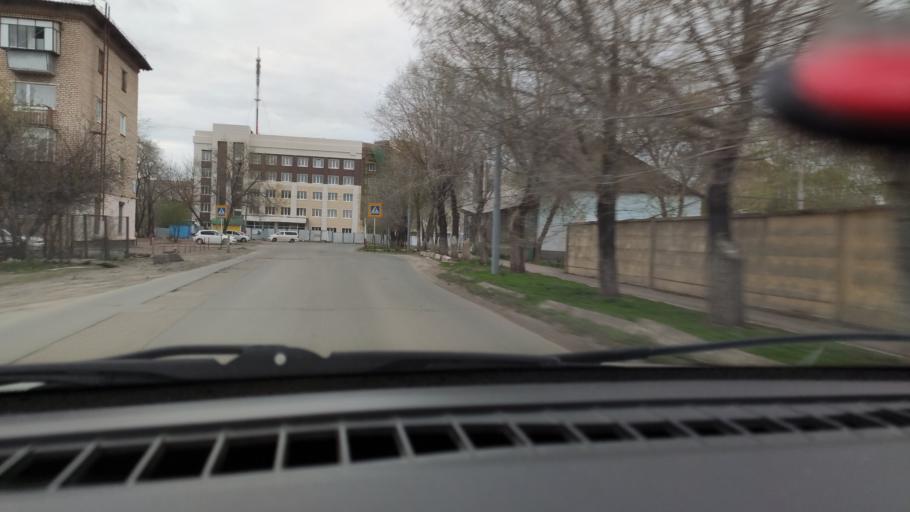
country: RU
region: Orenburg
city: Orenburg
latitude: 51.7754
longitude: 55.1246
